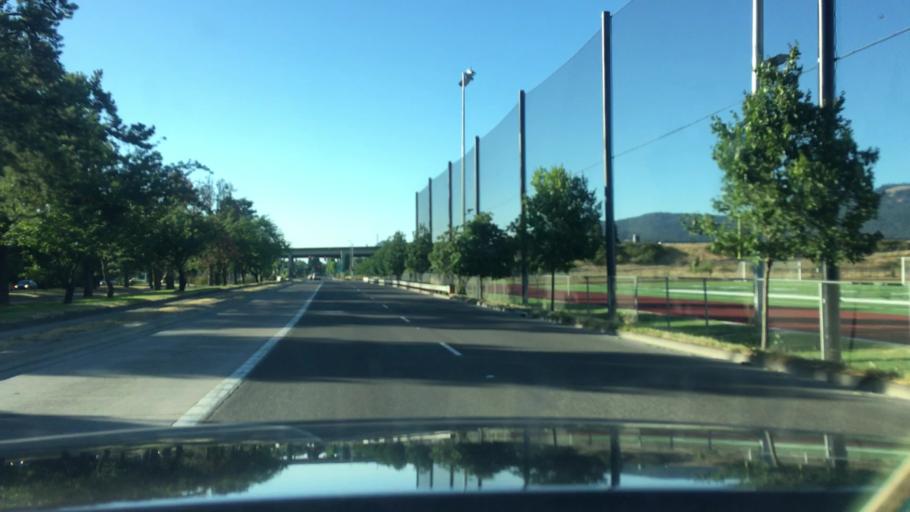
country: US
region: Oregon
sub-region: Lane County
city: Springfield
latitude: 44.0586
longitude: -123.0245
